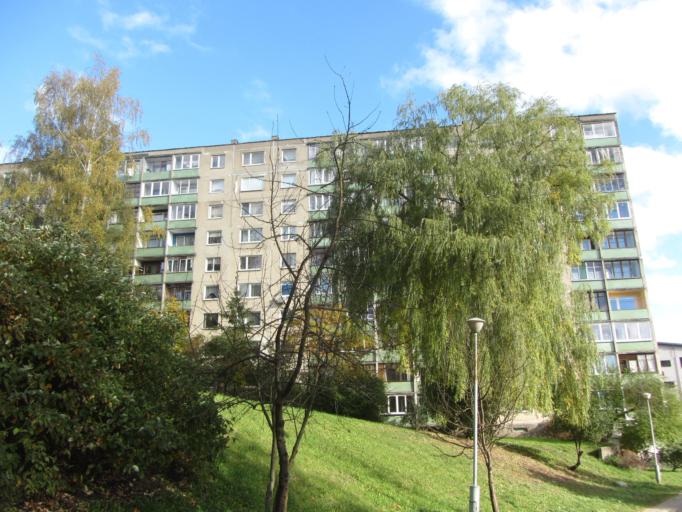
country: LT
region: Vilnius County
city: Lazdynai
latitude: 54.6720
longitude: 25.2109
